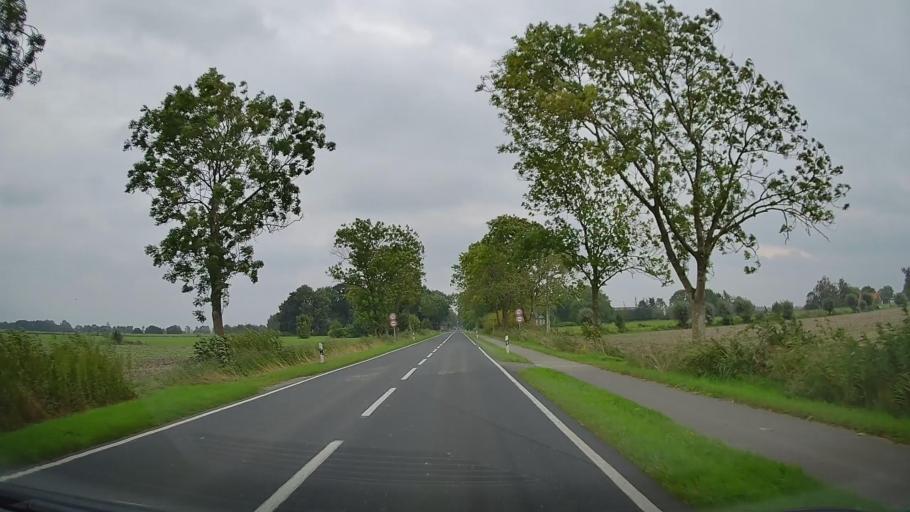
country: DE
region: Lower Saxony
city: Freiburg
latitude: 53.8140
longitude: 9.3012
